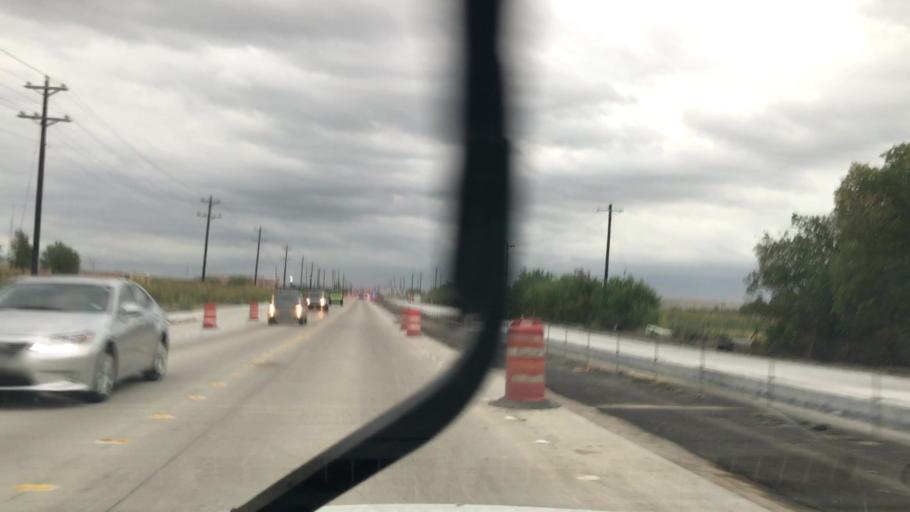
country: US
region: Texas
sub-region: Denton County
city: The Colony
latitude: 33.0447
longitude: -96.8876
